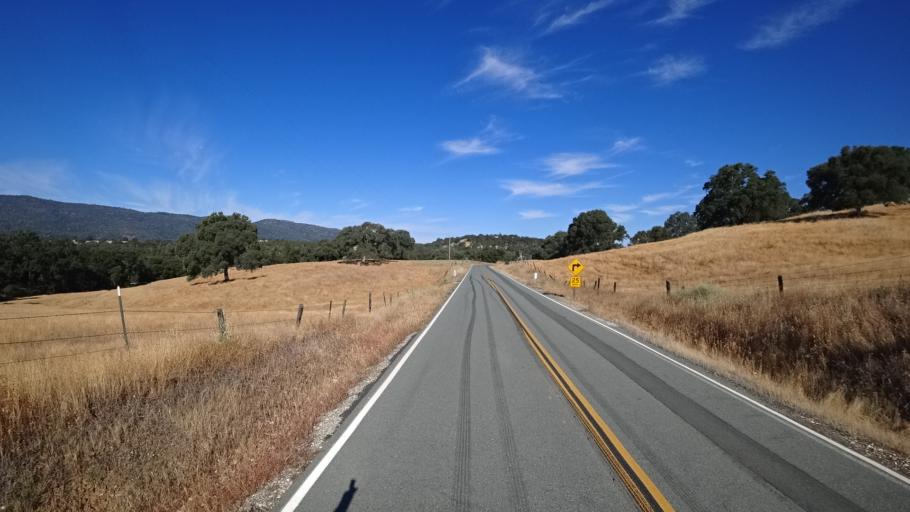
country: US
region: California
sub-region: Calaveras County
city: San Andreas
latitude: 38.1752
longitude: -120.6474
